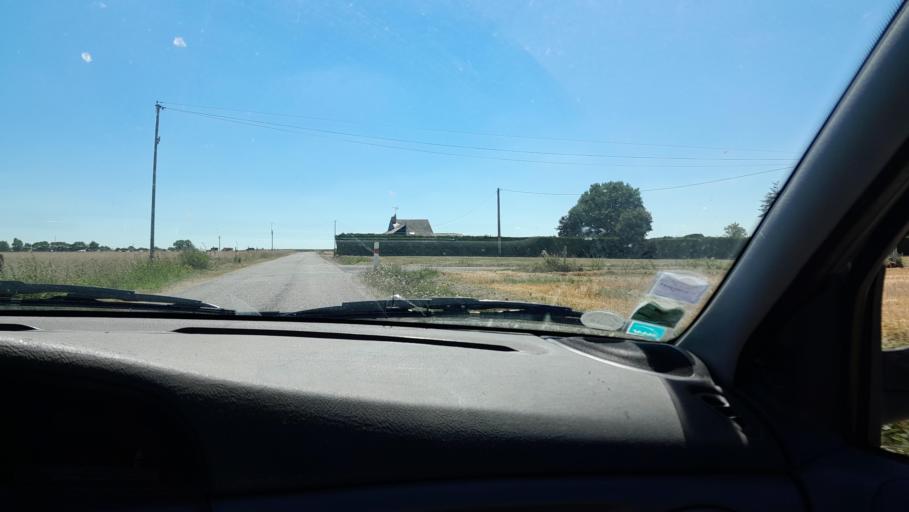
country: FR
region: Pays de la Loire
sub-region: Departement de Maine-et-Loire
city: Pouance
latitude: 47.8150
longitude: -1.1999
